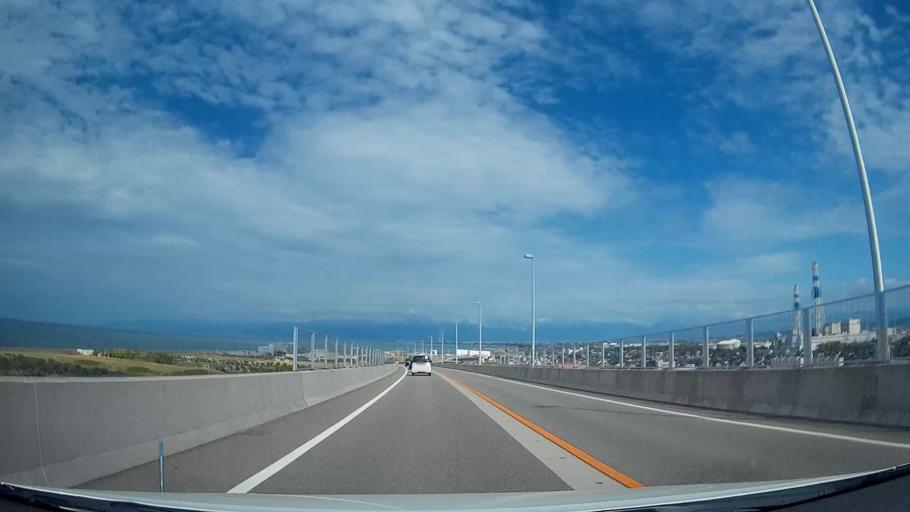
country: JP
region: Toyama
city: Nishishinminato
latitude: 36.7749
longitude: 137.1201
